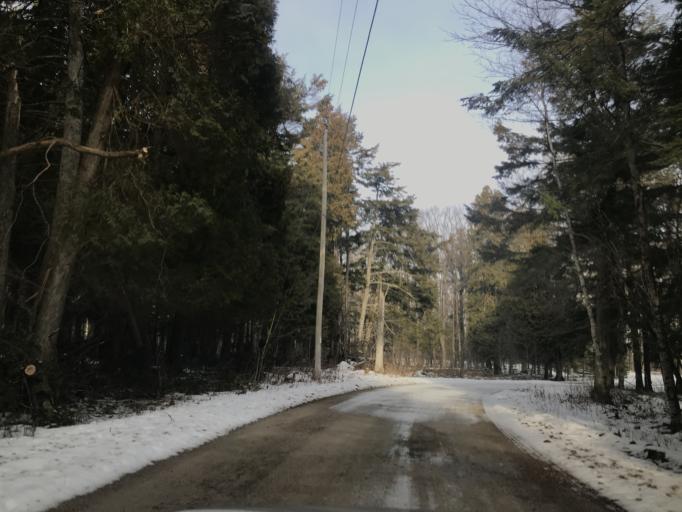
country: US
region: Wisconsin
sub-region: Door County
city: Sturgeon Bay
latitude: 45.1540
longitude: -87.0438
